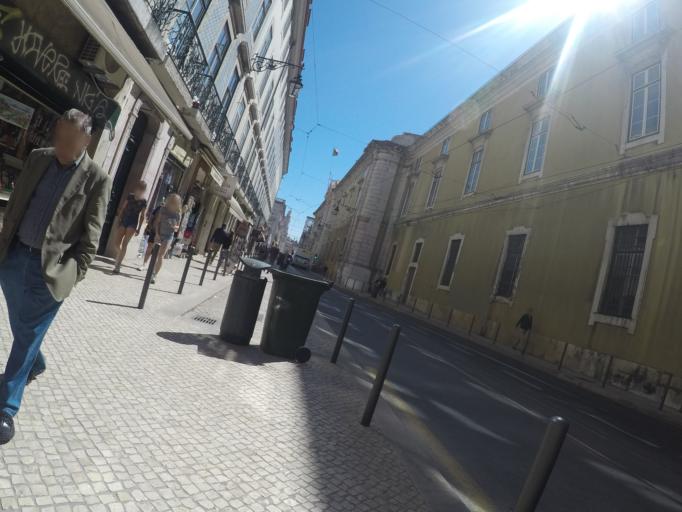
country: PT
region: Lisbon
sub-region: Lisbon
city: Lisbon
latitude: 38.7076
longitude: -9.1403
